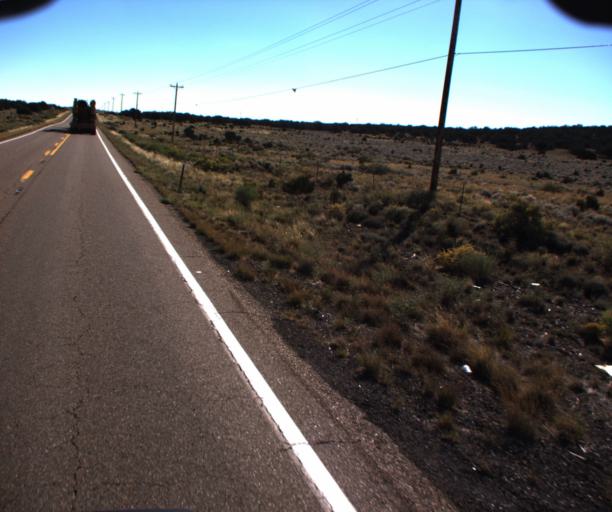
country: US
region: Arizona
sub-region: Apache County
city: Saint Johns
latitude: 34.4847
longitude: -109.5544
